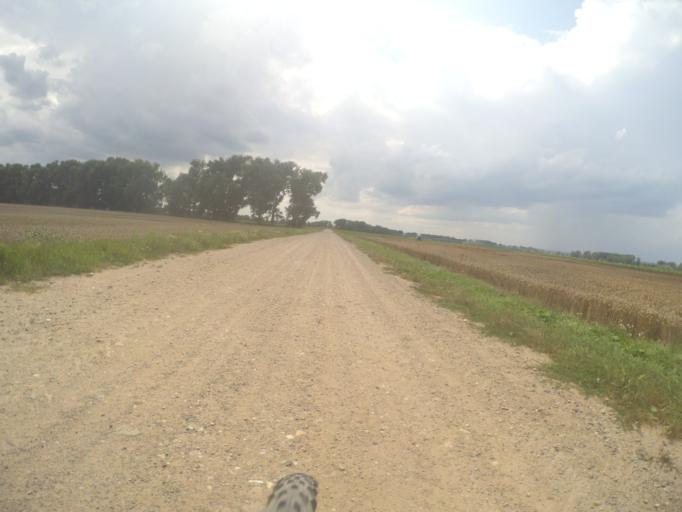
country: CZ
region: Central Bohemia
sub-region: Okres Melnik
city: Melnik
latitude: 50.3127
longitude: 14.4592
